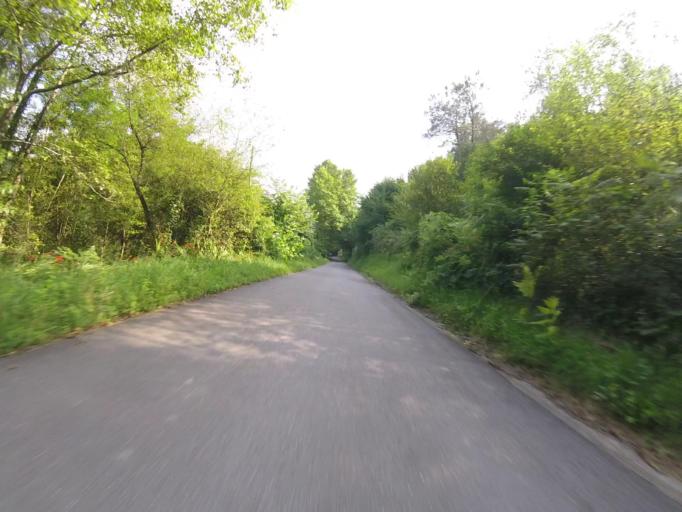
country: ES
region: Basque Country
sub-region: Provincia de Guipuzcoa
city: Astigarraga
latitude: 43.2542
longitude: -1.9500
